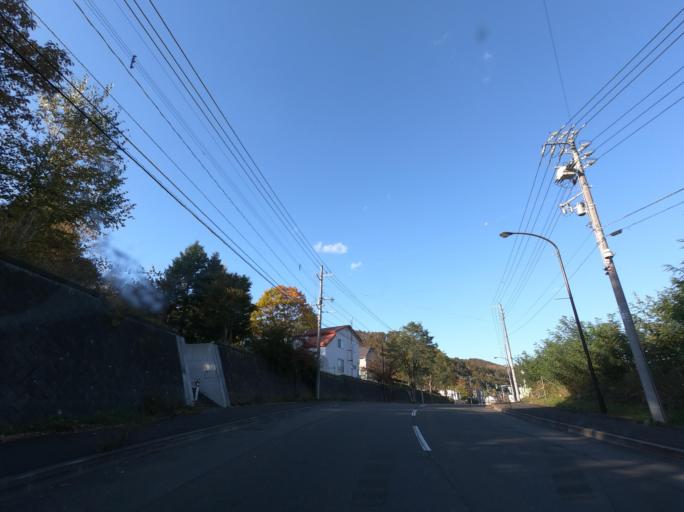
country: JP
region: Hokkaido
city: Iwamizawa
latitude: 43.0450
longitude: 141.9628
